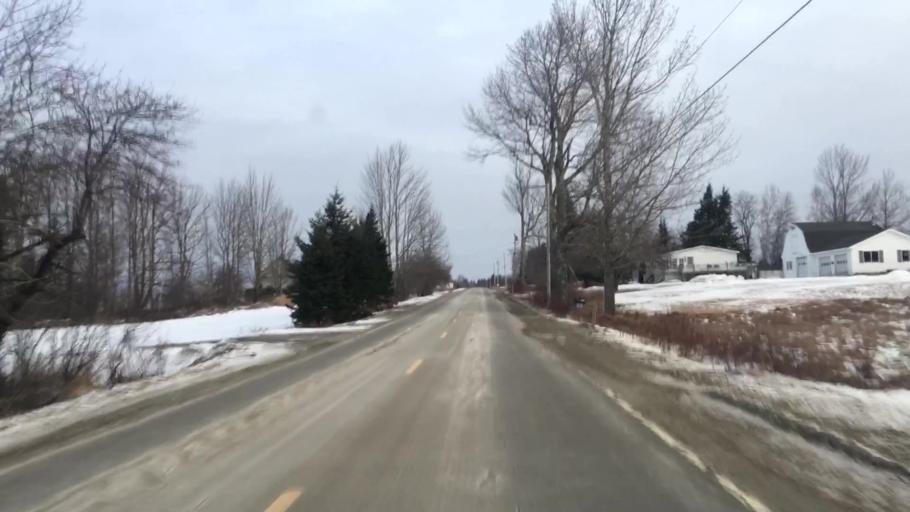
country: US
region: Maine
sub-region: Hancock County
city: Franklin
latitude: 44.7148
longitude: -68.3372
